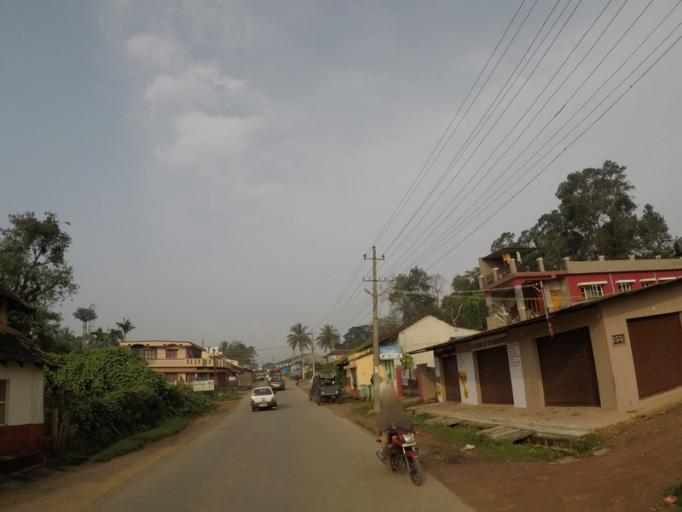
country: IN
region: Karnataka
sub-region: Chikmagalur
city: Mudigere
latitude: 13.2455
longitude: 75.6553
